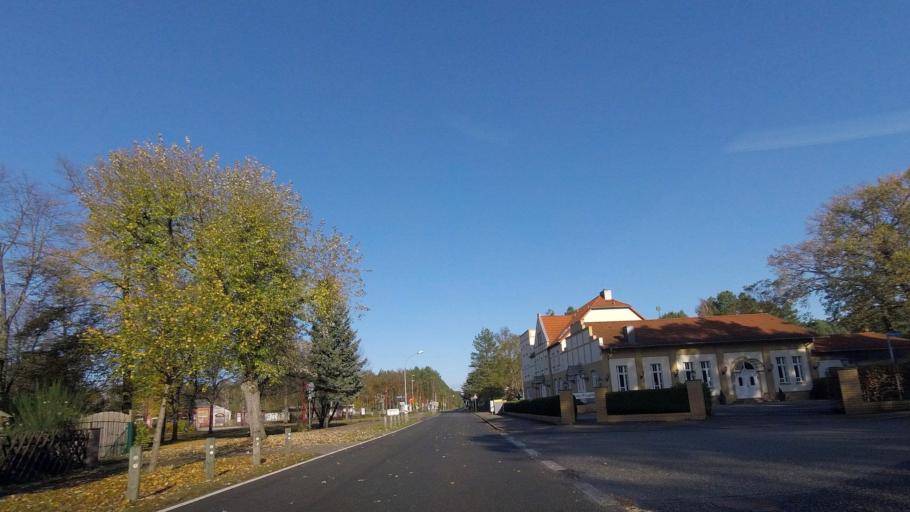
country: DE
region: Brandenburg
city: Borkheide
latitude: 52.2300
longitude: 12.8557
